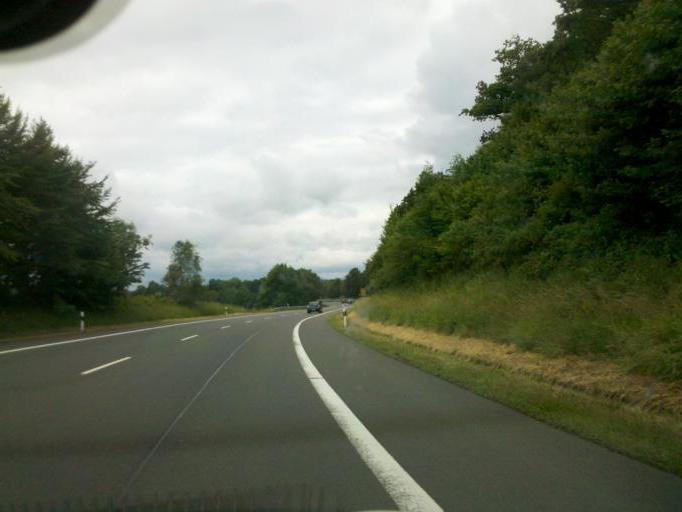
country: DE
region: North Rhine-Westphalia
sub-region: Regierungsbezirk Arnsberg
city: Olpe
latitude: 51.0458
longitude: 7.8640
